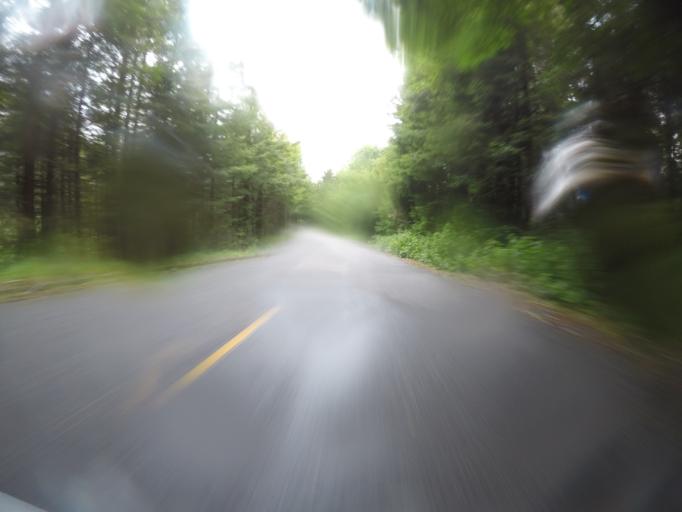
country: US
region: California
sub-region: Humboldt County
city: Westhaven-Moonstone
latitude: 41.3017
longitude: -124.0380
